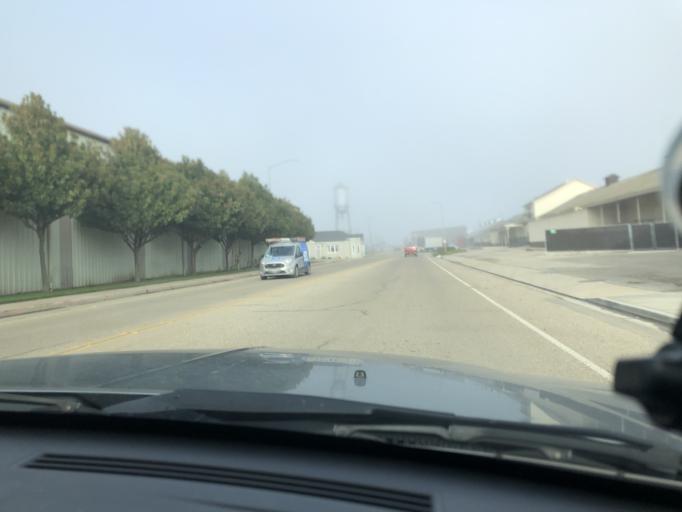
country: US
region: California
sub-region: Monterey County
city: King City
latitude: 36.2154
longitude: -121.1244
